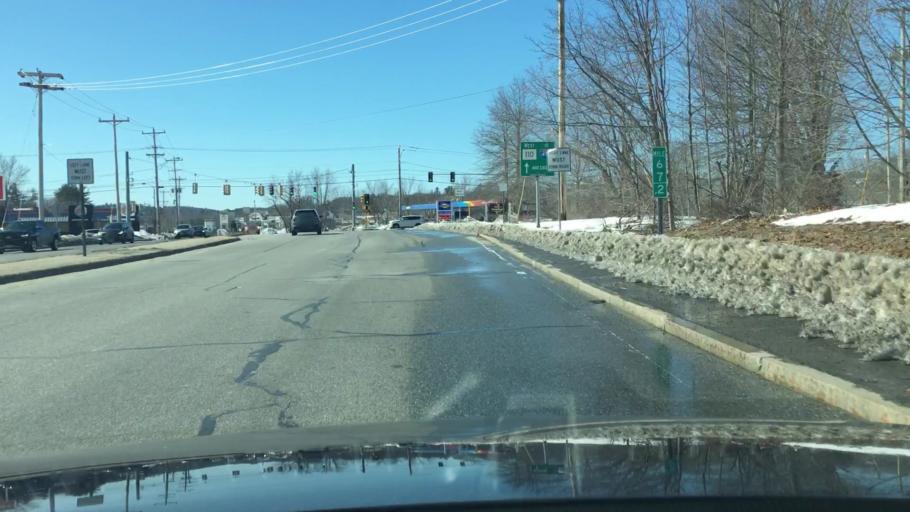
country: US
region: Massachusetts
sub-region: Essex County
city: Amesbury
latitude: 42.8459
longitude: -70.9054
